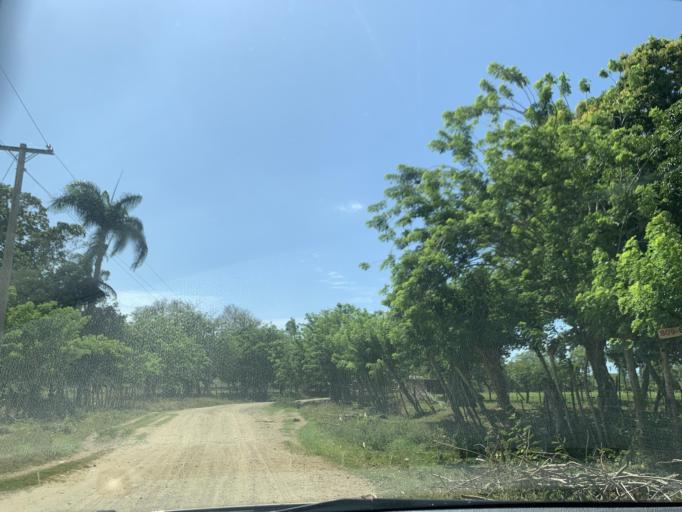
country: DO
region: Puerto Plata
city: Luperon
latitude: 19.8867
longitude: -70.8742
